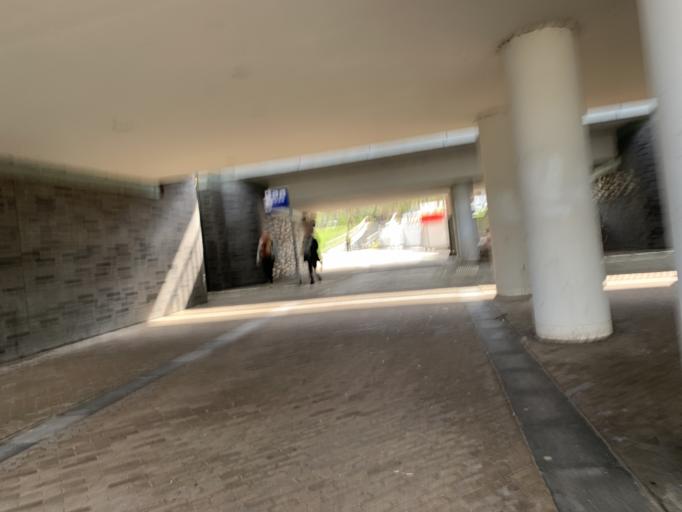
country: NL
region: Groningen
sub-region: Gemeente Groningen
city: Oosterpark
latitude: 53.2048
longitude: 6.5859
